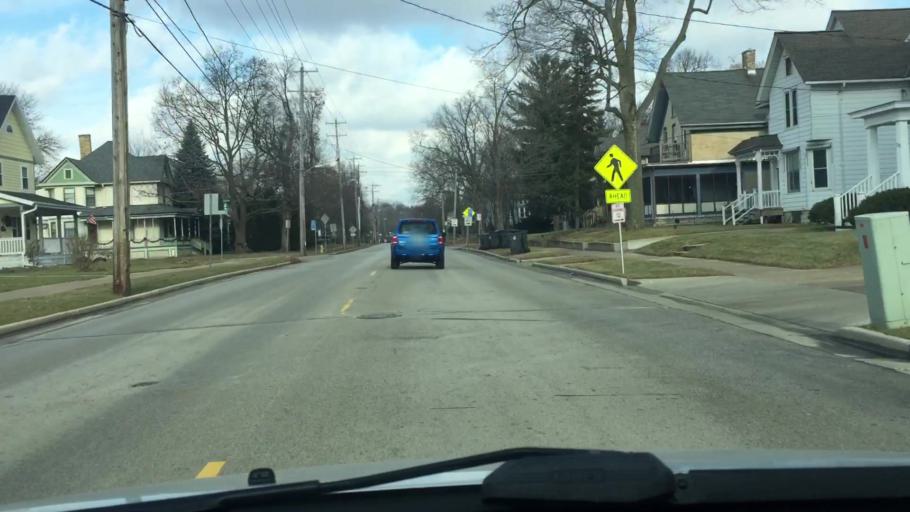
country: US
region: Wisconsin
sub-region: Waukesha County
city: Waukesha
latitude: 43.0067
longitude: -88.2366
